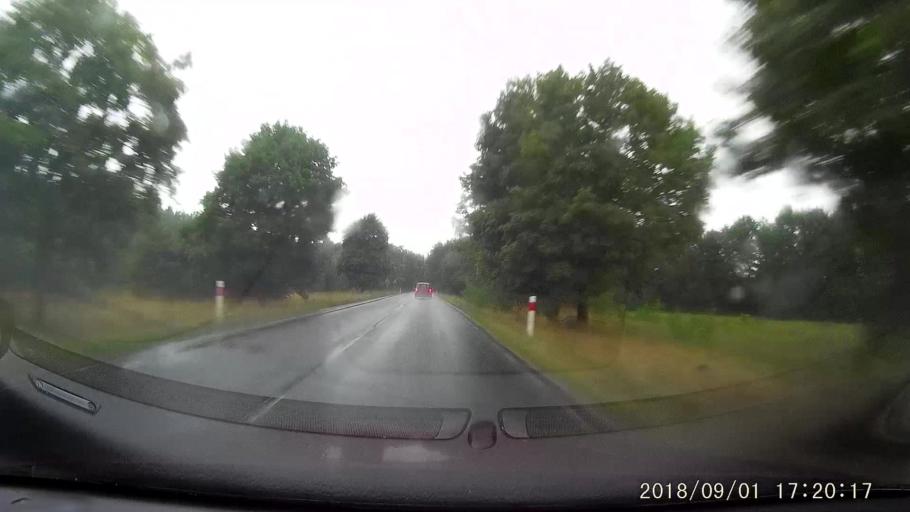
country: PL
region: Lubusz
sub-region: Powiat zielonogorski
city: Nowogrod Bobrzanski
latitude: 51.7257
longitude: 15.2781
